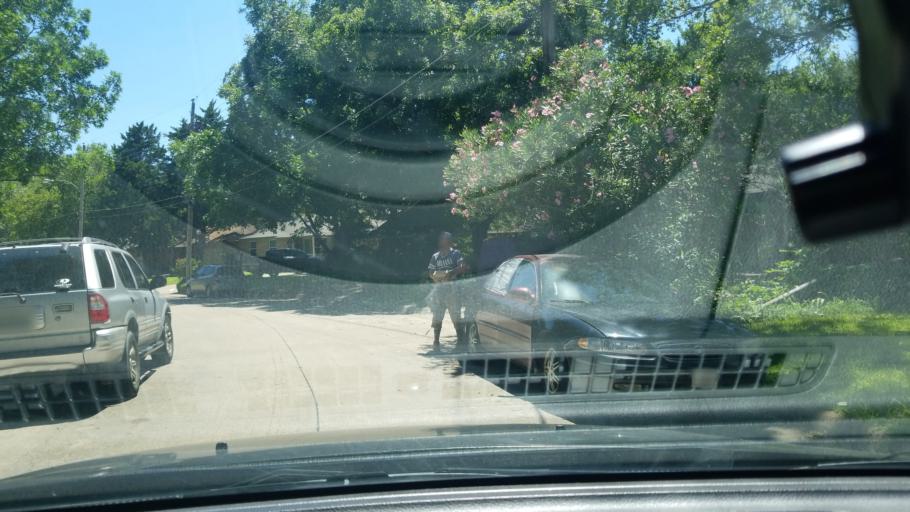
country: US
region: Texas
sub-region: Dallas County
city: Mesquite
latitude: 32.7573
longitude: -96.6070
